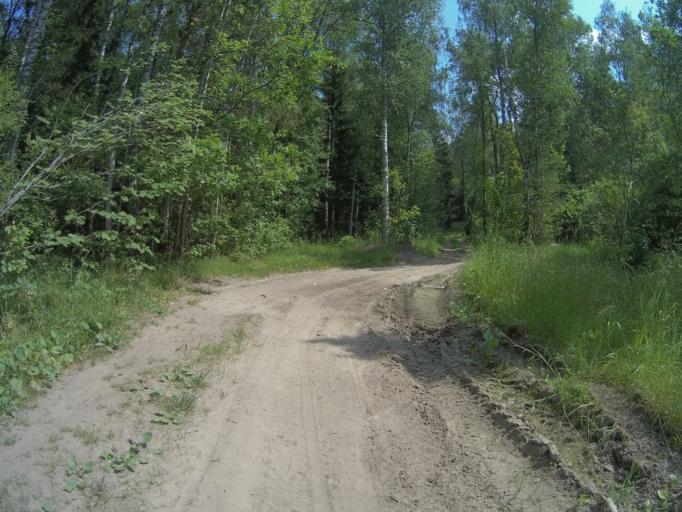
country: RU
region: Vladimir
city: Kommunar
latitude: 56.0347
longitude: 40.5090
